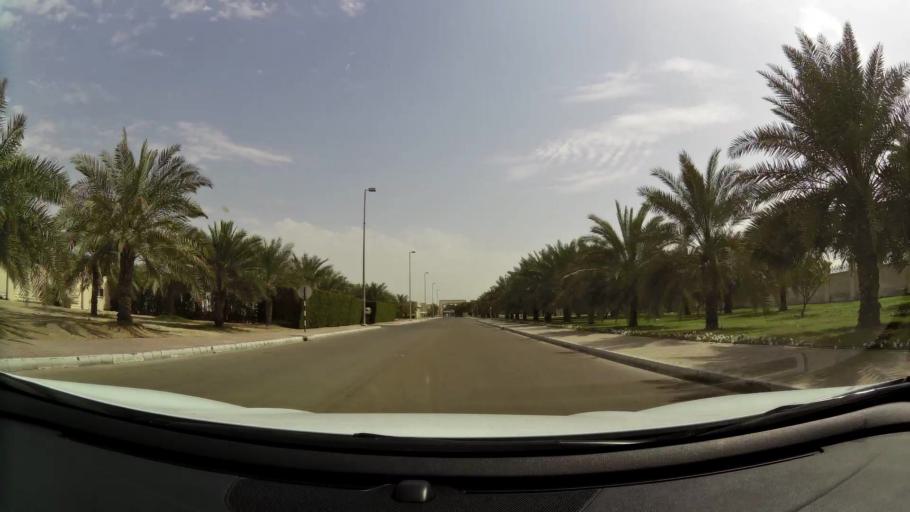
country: AE
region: Abu Dhabi
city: Abu Dhabi
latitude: 24.4488
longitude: 54.3486
